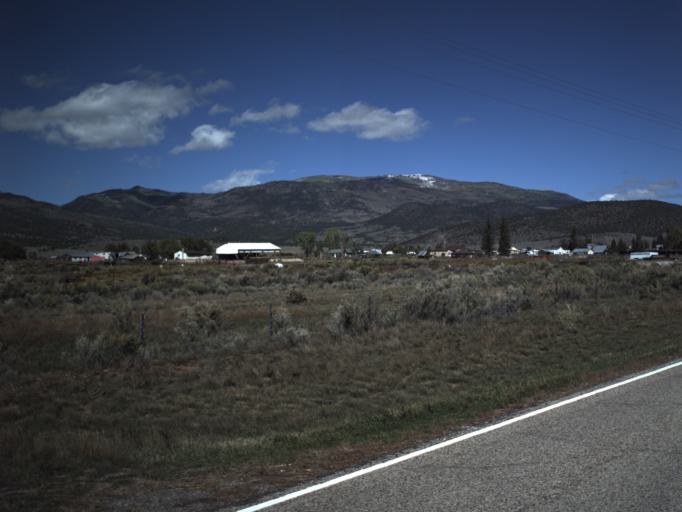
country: US
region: Utah
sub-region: Wayne County
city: Loa
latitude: 38.5030
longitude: -111.8813
